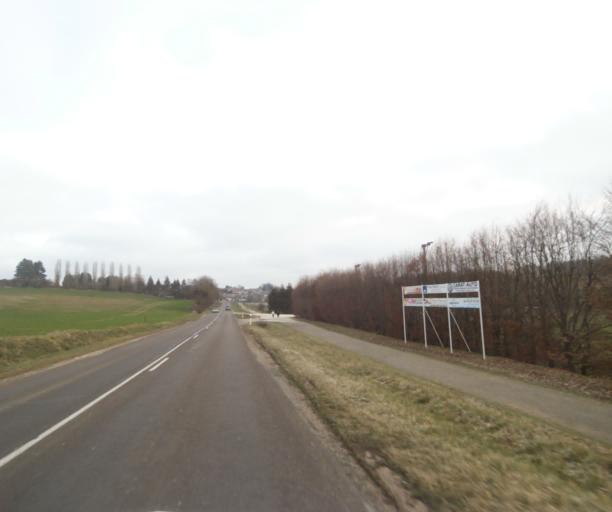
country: FR
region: Champagne-Ardenne
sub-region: Departement de la Haute-Marne
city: Chancenay
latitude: 48.6637
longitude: 4.9779
